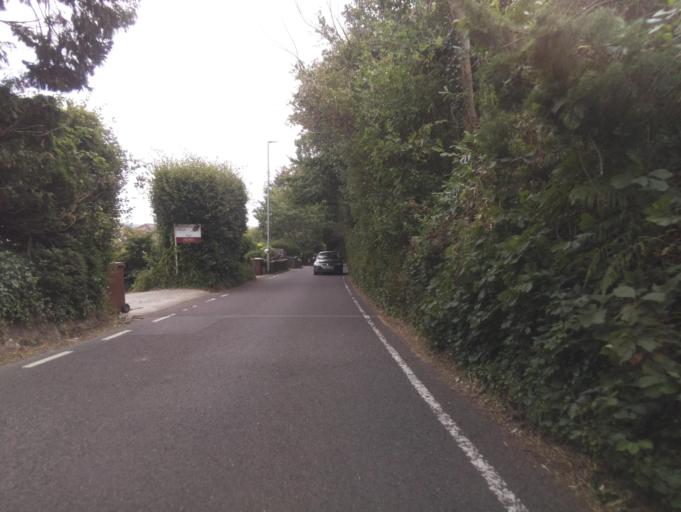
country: GB
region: England
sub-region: Devon
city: Totnes
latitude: 50.4326
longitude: -3.7144
